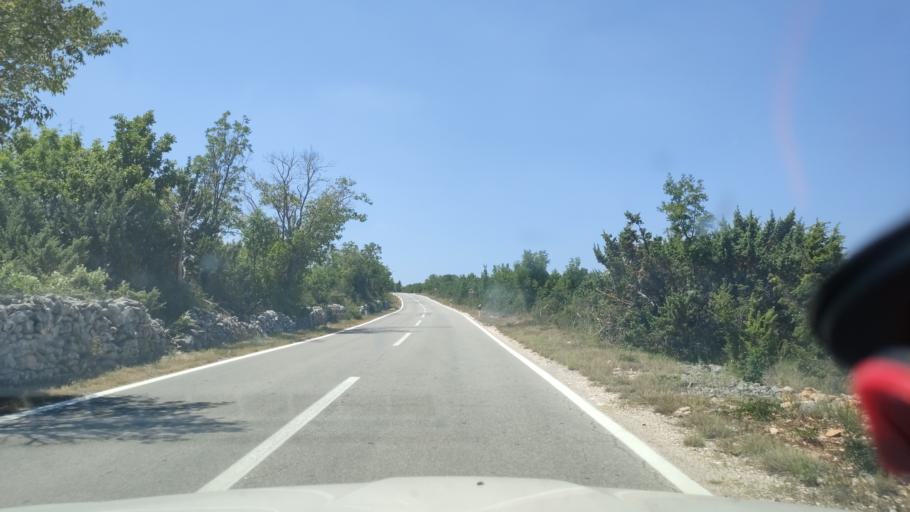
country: HR
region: Sibensko-Kniniska
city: Kistanje
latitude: 44.0075
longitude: 16.0032
